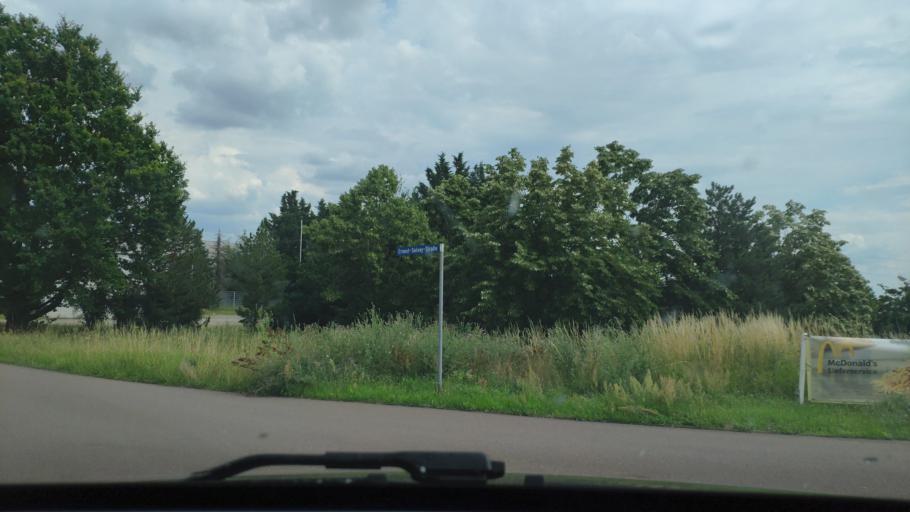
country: DE
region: Saxony-Anhalt
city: Bernburg
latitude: 51.7738
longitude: 11.7497
